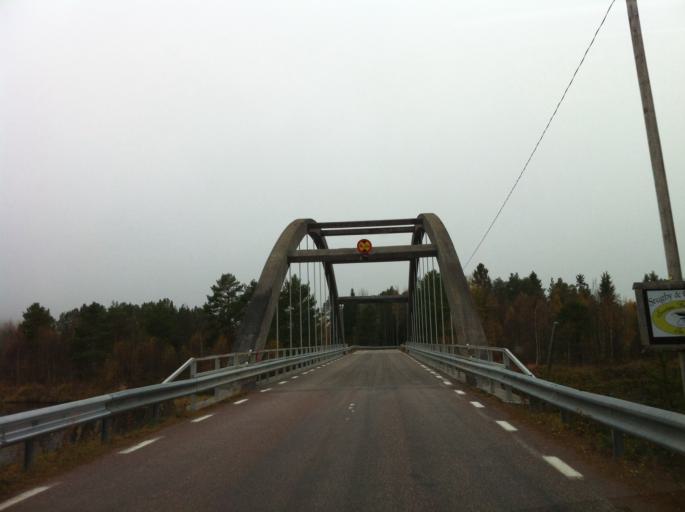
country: NO
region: Hedmark
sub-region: Trysil
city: Innbygda
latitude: 61.8570
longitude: 12.7115
